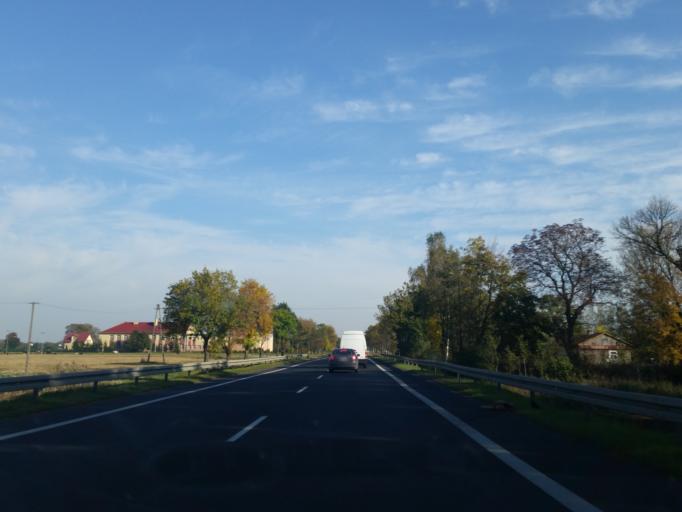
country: PL
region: Masovian Voivodeship
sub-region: Powiat sierpecki
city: Zawidz
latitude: 52.8093
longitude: 19.8258
